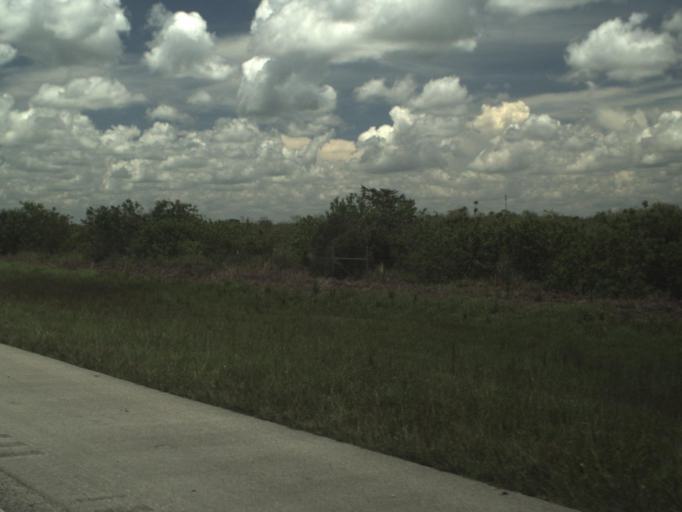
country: US
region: Florida
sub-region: Broward County
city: Weston
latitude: 26.1650
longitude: -80.8181
